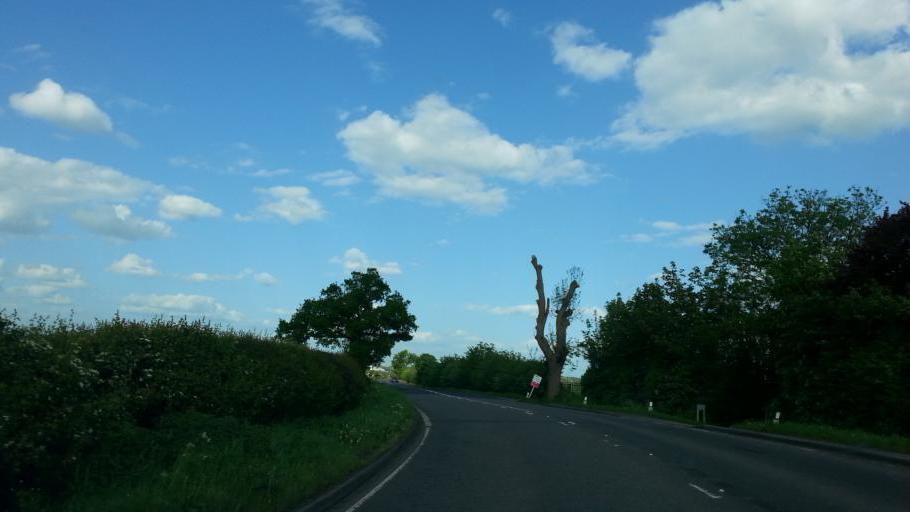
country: GB
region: England
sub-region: Lincolnshire
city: Gainsborough
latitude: 53.3754
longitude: -0.8277
